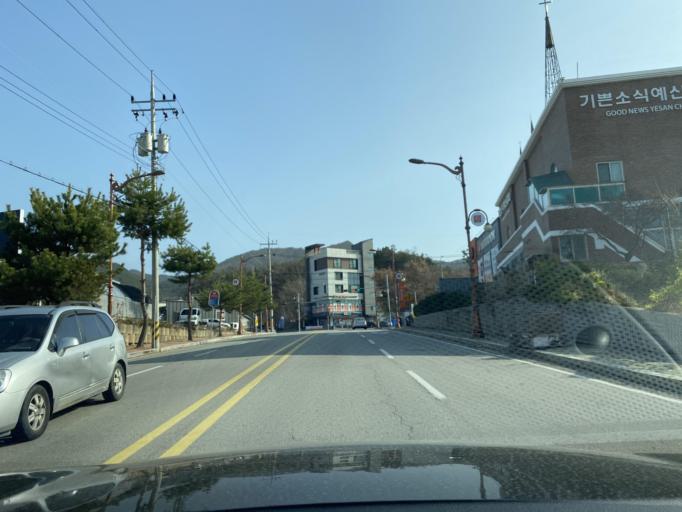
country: KR
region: Chungcheongnam-do
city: Yesan
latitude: 36.6979
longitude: 126.8363
